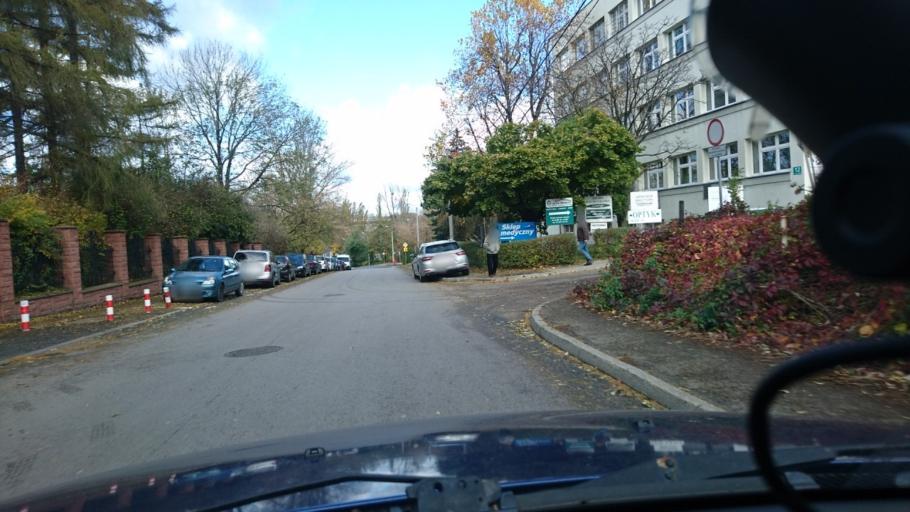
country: PL
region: Silesian Voivodeship
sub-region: Bielsko-Biala
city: Bielsko-Biala
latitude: 49.8311
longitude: 19.0416
